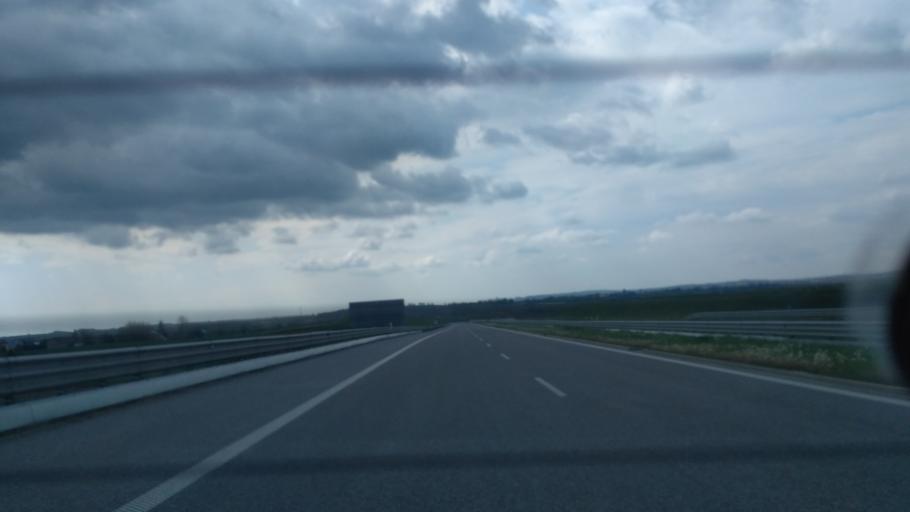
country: PL
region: Subcarpathian Voivodeship
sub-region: Powiat jaroslawski
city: Pawlosiow
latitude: 49.9581
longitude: 22.6602
